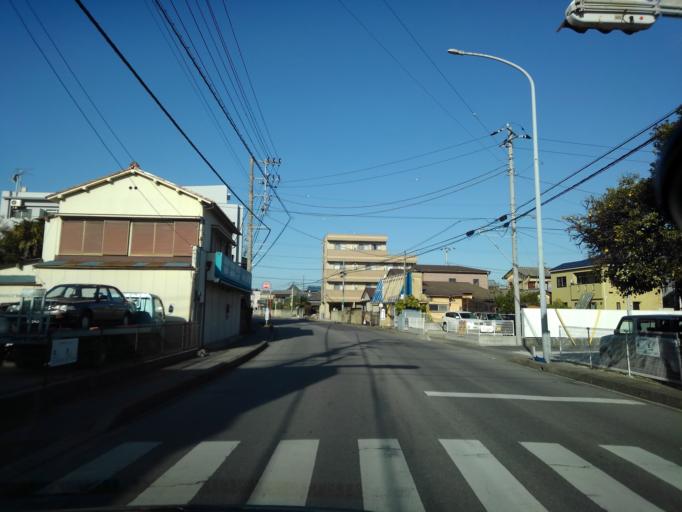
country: JP
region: Chiba
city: Funabashi
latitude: 35.6602
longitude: 140.0519
